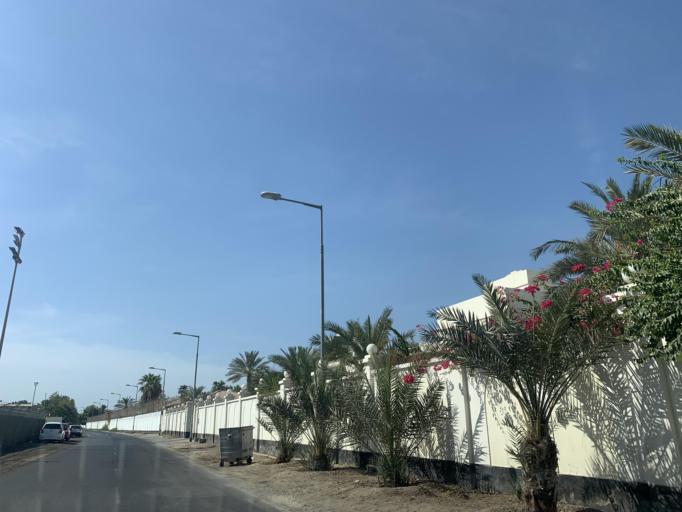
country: BH
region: Northern
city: Madinat `Isa
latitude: 26.1928
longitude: 50.4722
